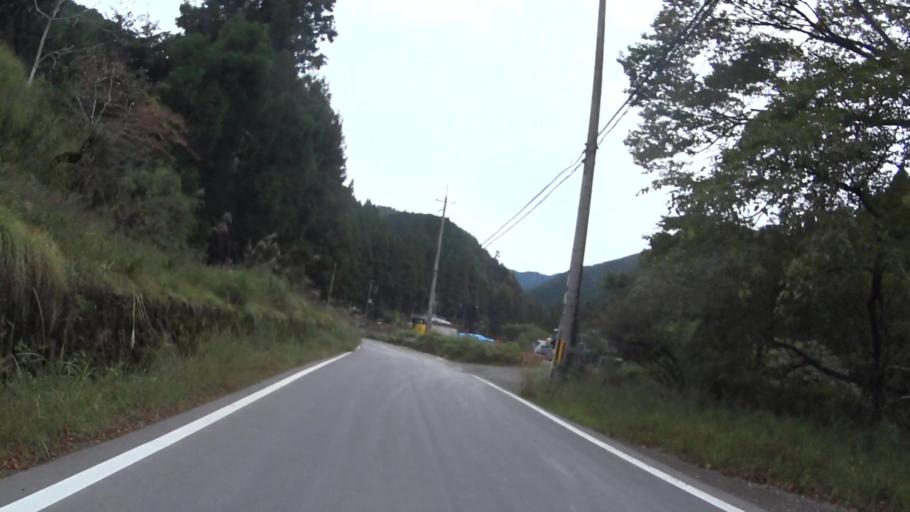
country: JP
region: Kyoto
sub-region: Kyoto-shi
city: Kamigyo-ku
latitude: 35.1259
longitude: 135.7782
